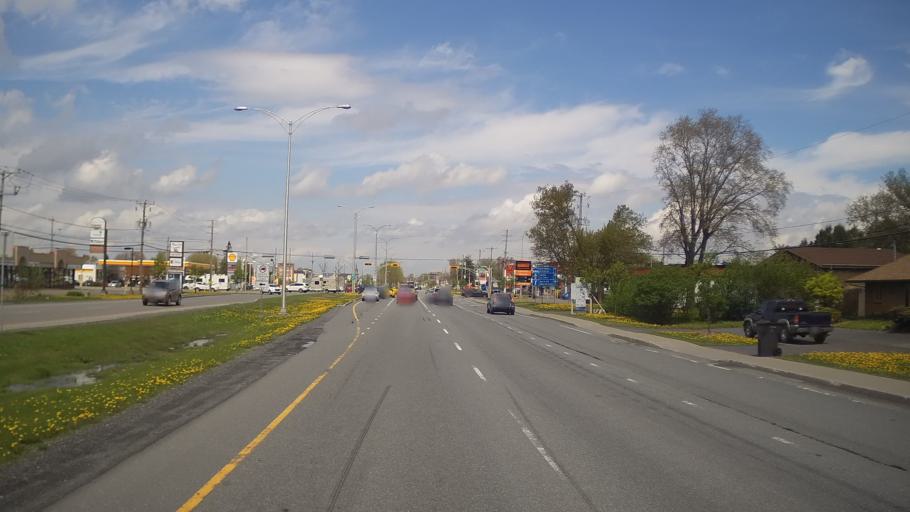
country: CA
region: Quebec
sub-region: Monteregie
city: Saint-Jean-sur-Richelieu
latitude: 45.3509
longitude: -73.2922
